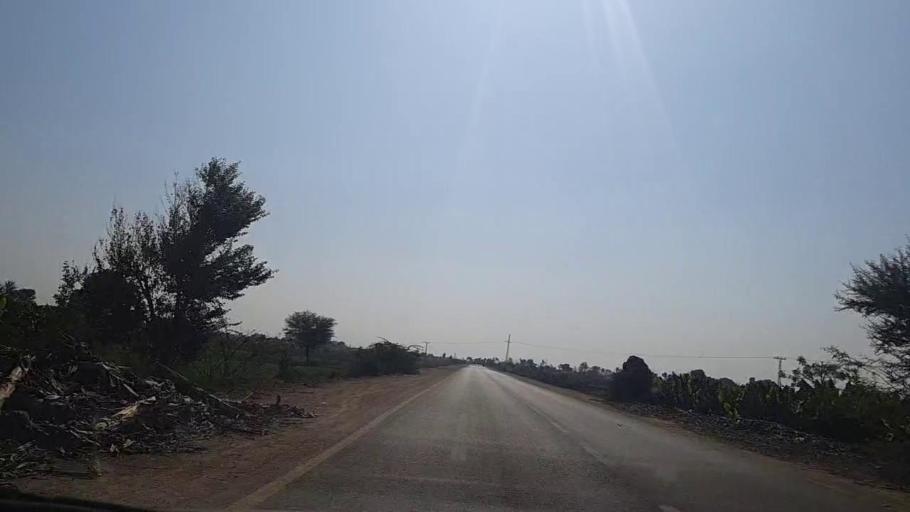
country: PK
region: Sindh
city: Sakrand
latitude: 26.1006
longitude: 68.4035
